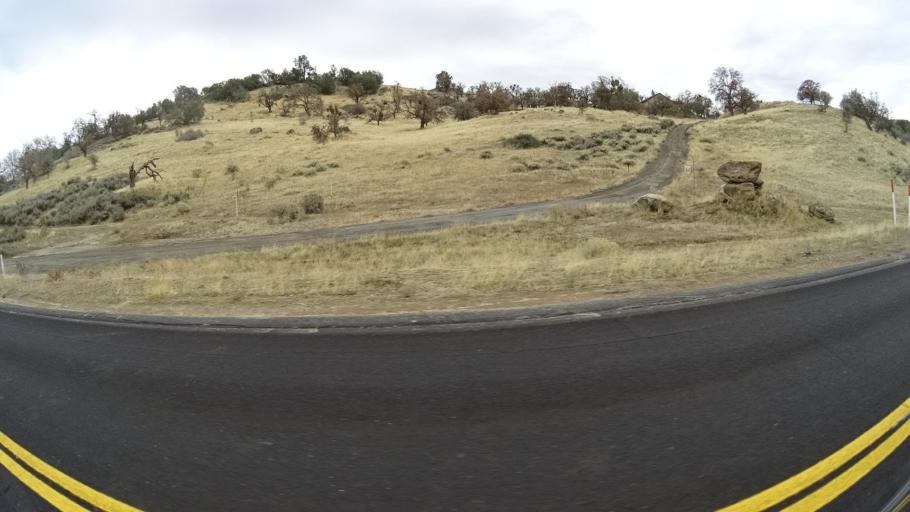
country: US
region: California
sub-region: Kern County
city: Stallion Springs
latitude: 35.0944
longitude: -118.6584
